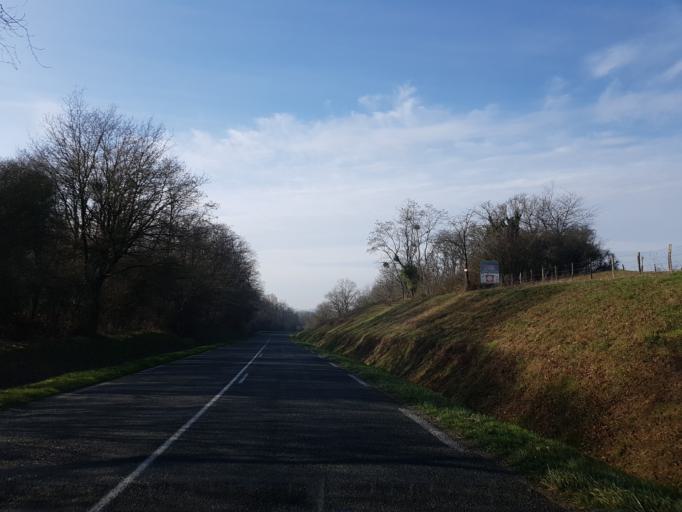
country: FR
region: Bourgogne
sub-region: Departement de Saone-et-Loire
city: La Motte-Saint-Jean
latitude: 46.5965
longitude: 3.9520
